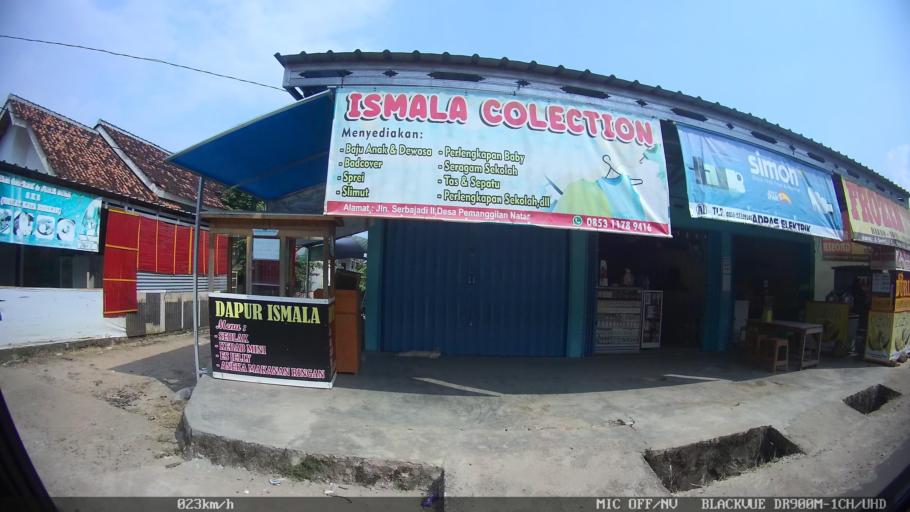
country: ID
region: Lampung
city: Natar
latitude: -5.3464
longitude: 105.2238
